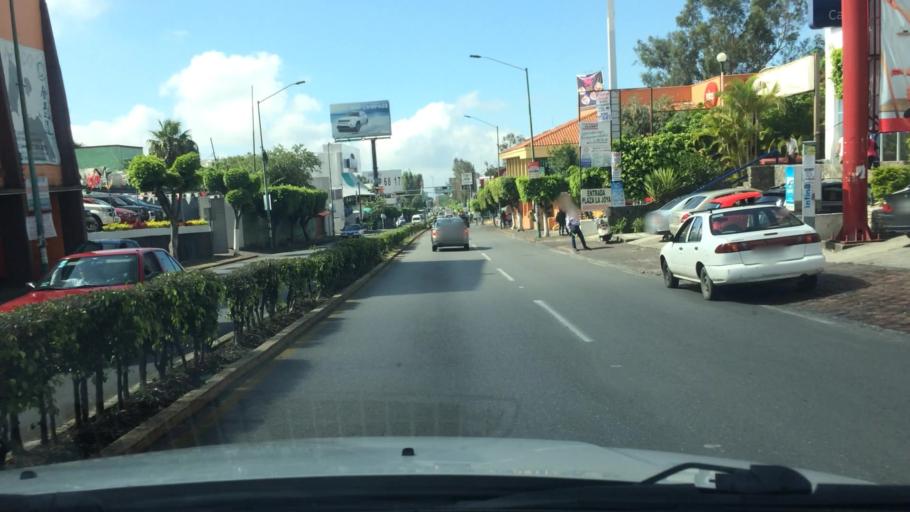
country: MX
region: Morelos
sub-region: Cuernavaca
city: Fraccionamiento Lomas de Ahuatlan
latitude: 18.9577
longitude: -99.2458
